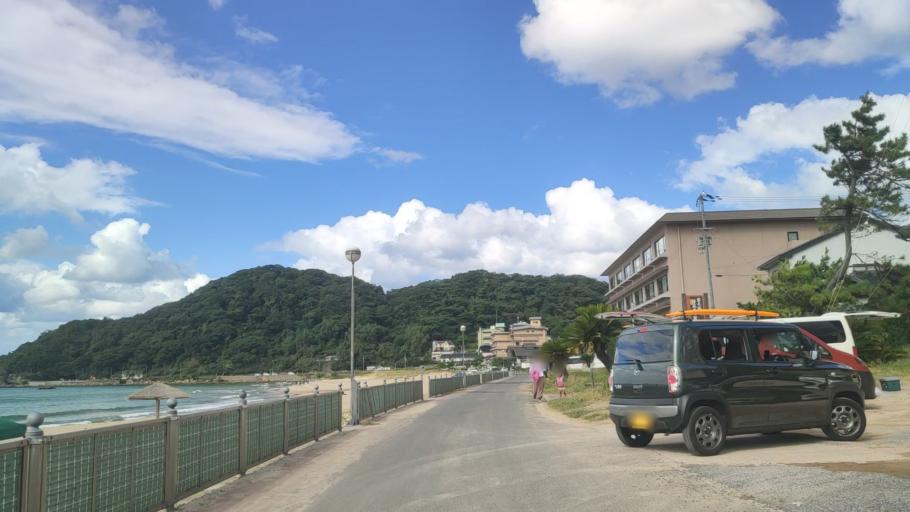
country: JP
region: Hyogo
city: Toyooka
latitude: 35.6651
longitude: 134.9666
